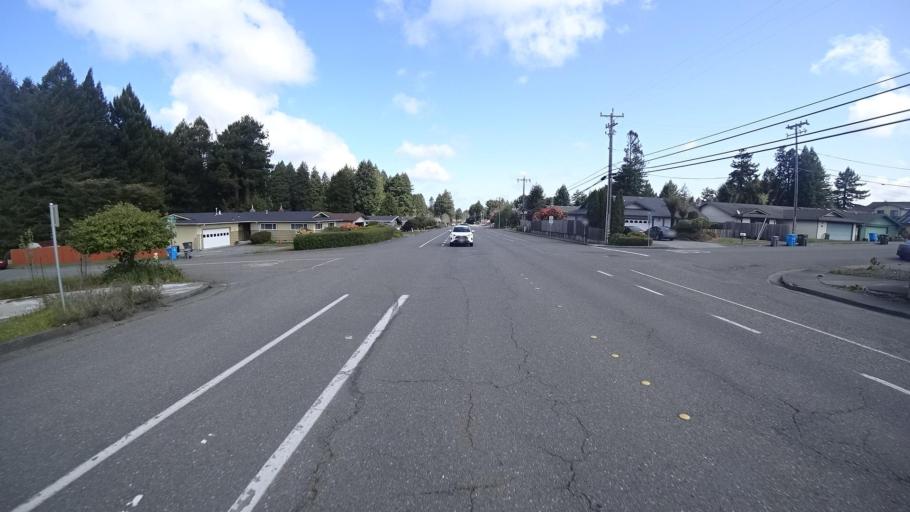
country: US
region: California
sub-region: Humboldt County
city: Pine Hills
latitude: 40.7405
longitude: -124.1475
